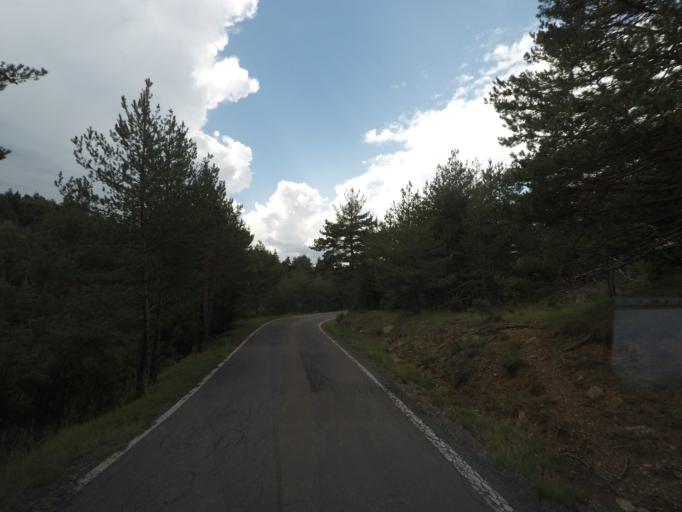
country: ES
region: Aragon
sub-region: Provincia de Huesca
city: Fiscal
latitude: 42.4081
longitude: -0.0914
